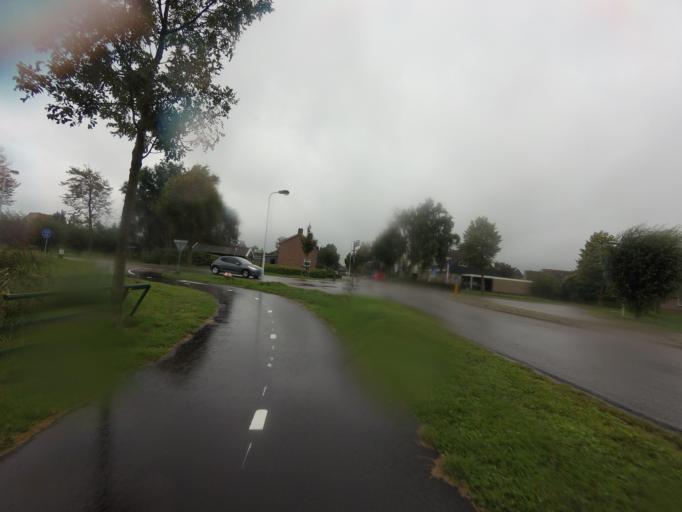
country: NL
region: Friesland
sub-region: Gemeente Tytsjerksteradiel
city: Garyp
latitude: 53.1324
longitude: 5.9413
